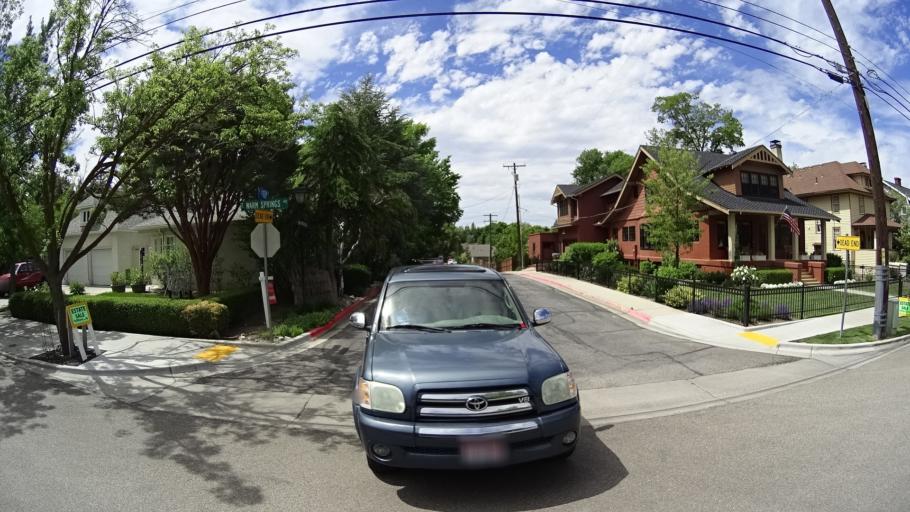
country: US
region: Idaho
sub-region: Ada County
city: Boise
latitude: 43.6046
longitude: -116.1770
